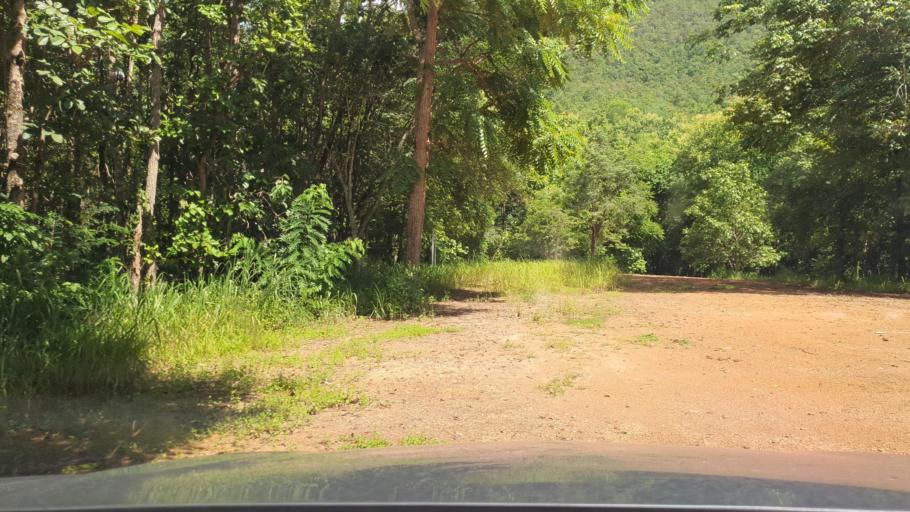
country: TH
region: Chiang Mai
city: Mae On
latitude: 18.7339
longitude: 99.2381
